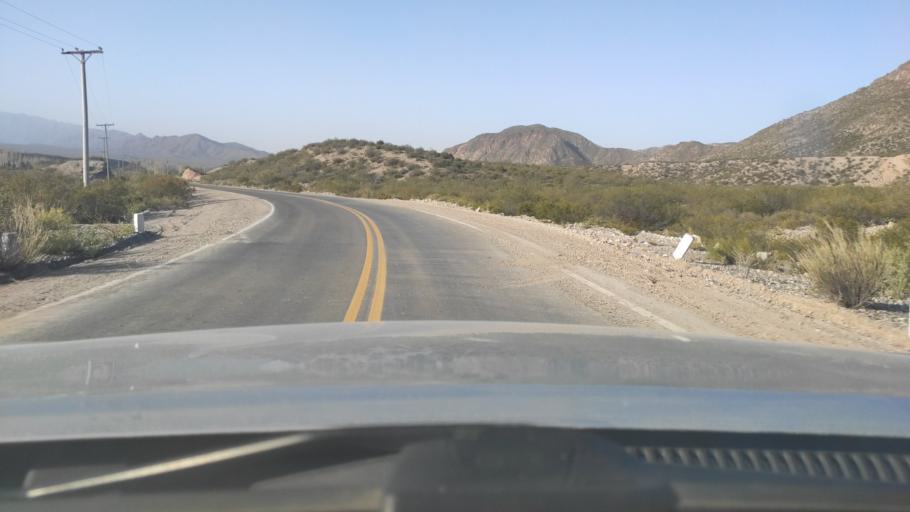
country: AR
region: San Juan
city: Villa Media Agua
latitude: -32.0079
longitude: -68.7699
